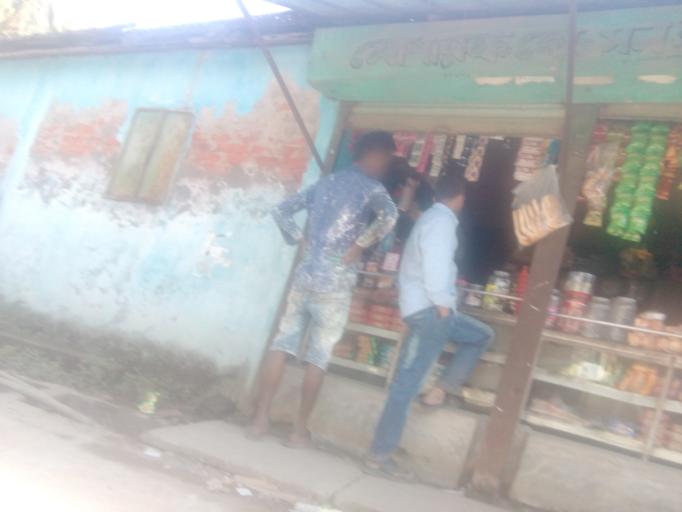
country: BD
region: Dhaka
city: Paltan
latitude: 23.7070
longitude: 90.4750
